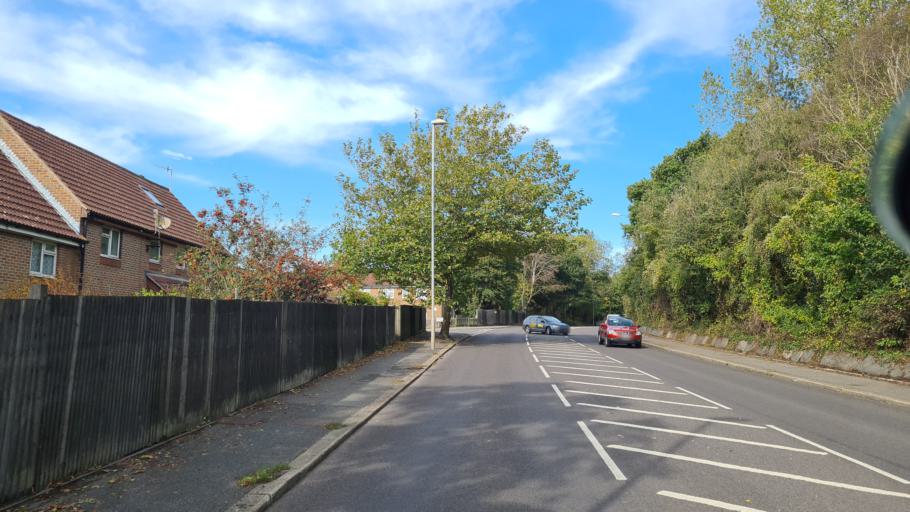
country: GB
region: England
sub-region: East Sussex
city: Saint Leonards-on-Sea
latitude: 50.8817
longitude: 0.5516
